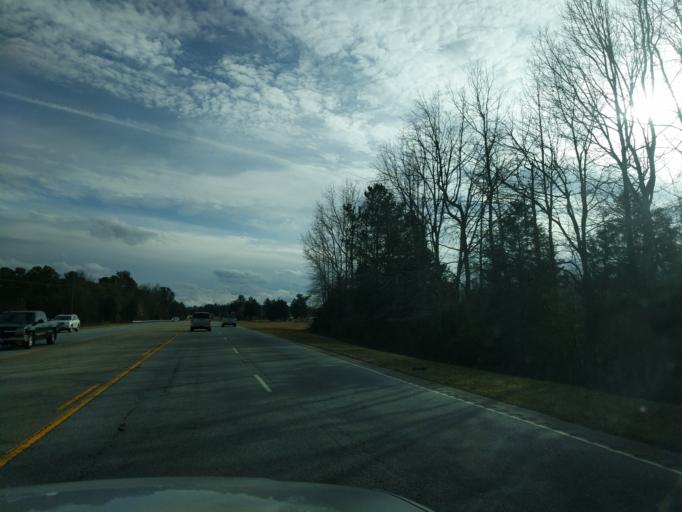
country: US
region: South Carolina
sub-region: Anderson County
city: Honea Path
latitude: 34.5343
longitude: -82.3161
